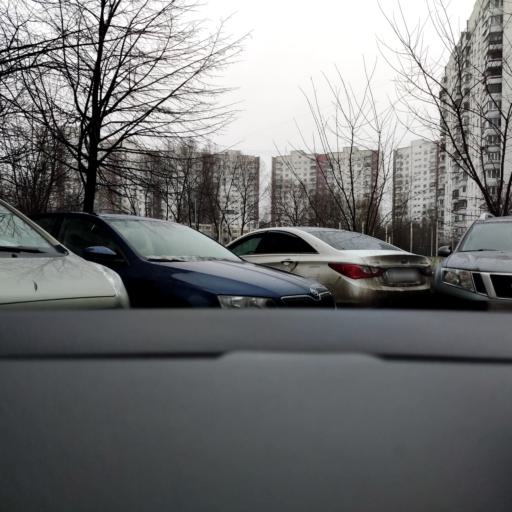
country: RU
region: Moskovskaya
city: Reutov
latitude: 55.7406
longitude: 37.8686
